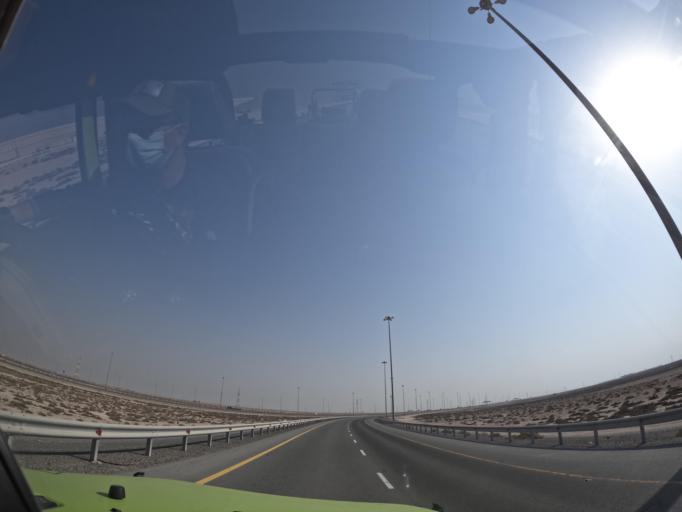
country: AE
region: Abu Dhabi
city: Abu Dhabi
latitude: 24.6757
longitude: 54.8117
